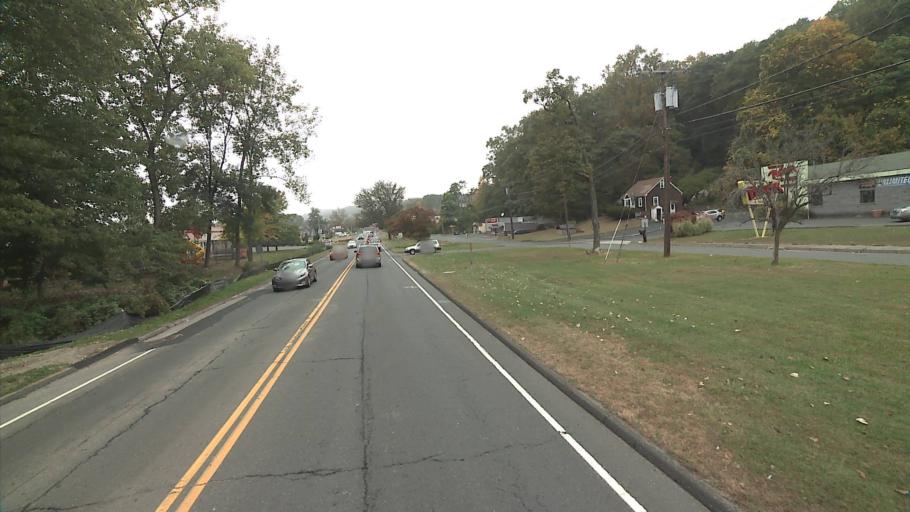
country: US
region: Connecticut
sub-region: Fairfield County
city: Danbury
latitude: 41.3915
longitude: -73.5051
